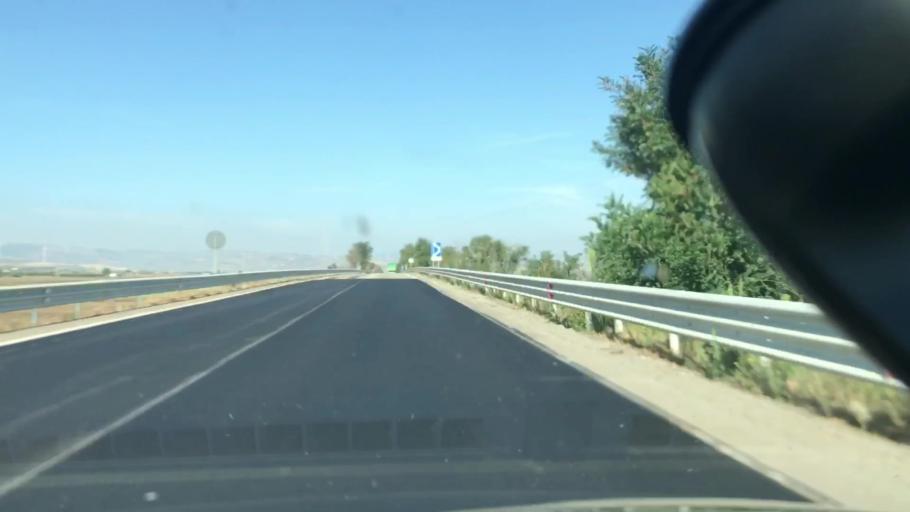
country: IT
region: Basilicate
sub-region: Provincia di Potenza
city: Zona 179
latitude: 41.0754
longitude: 15.6427
